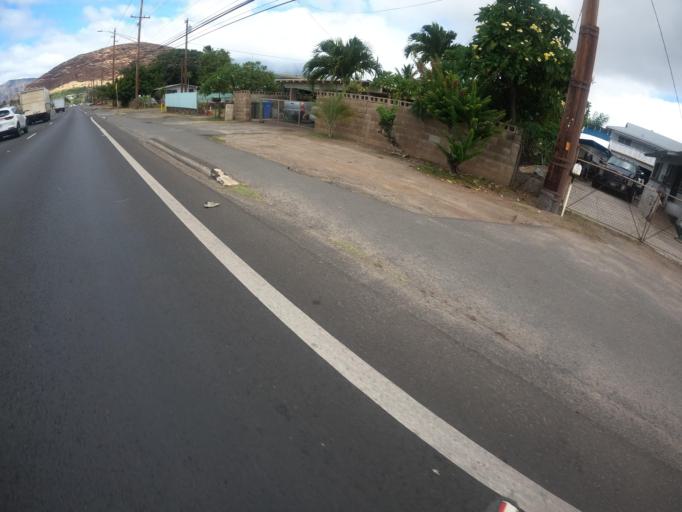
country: US
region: Hawaii
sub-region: Honolulu County
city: Ma'ili
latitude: 21.4207
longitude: -158.1773
